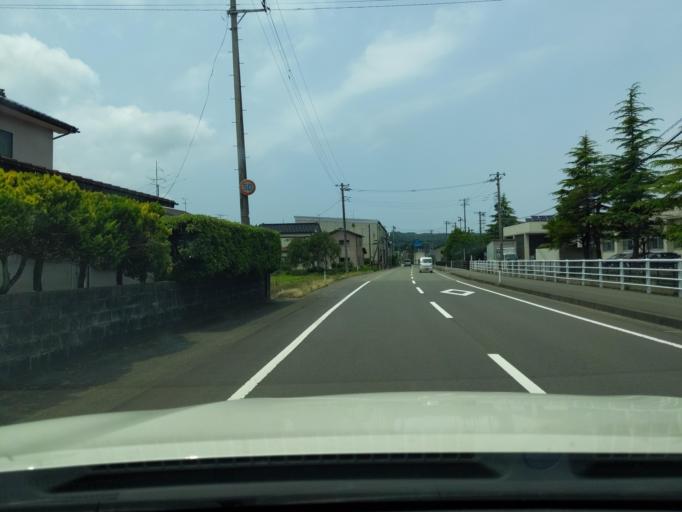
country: JP
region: Niigata
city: Kashiwazaki
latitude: 37.3308
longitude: 138.5661
